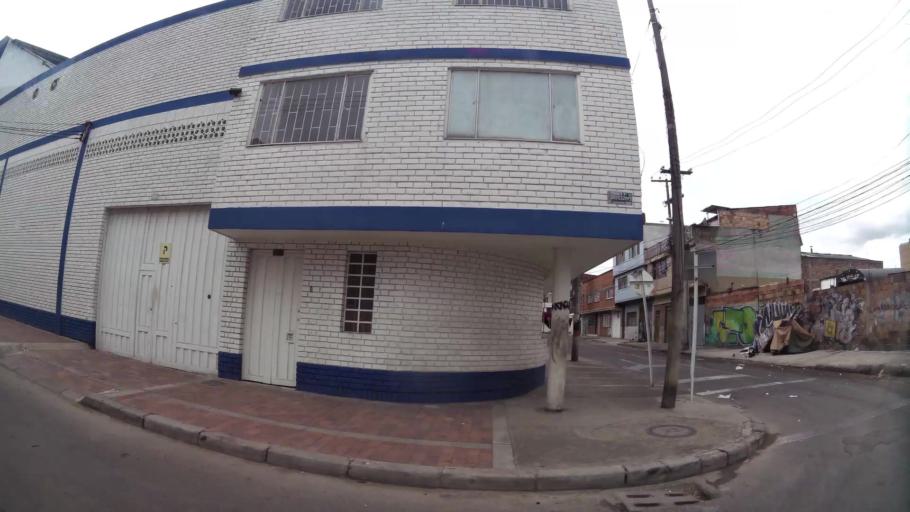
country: CO
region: Bogota D.C.
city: Bogota
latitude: 4.6071
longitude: -74.0997
